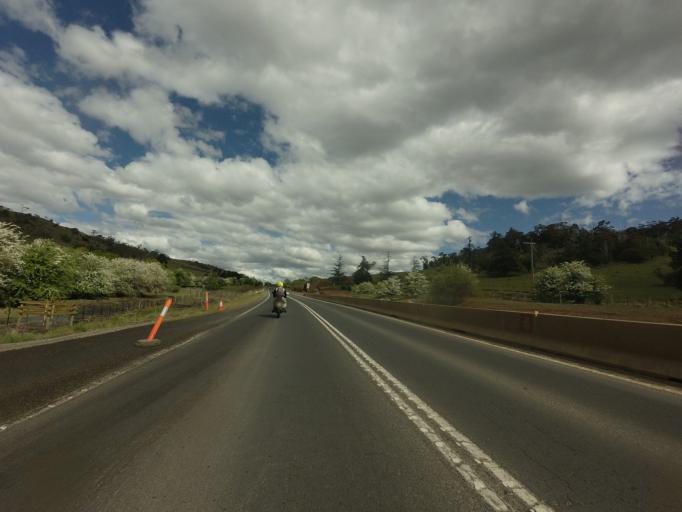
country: AU
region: Tasmania
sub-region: Brighton
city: Bridgewater
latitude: -42.2478
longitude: 147.4056
